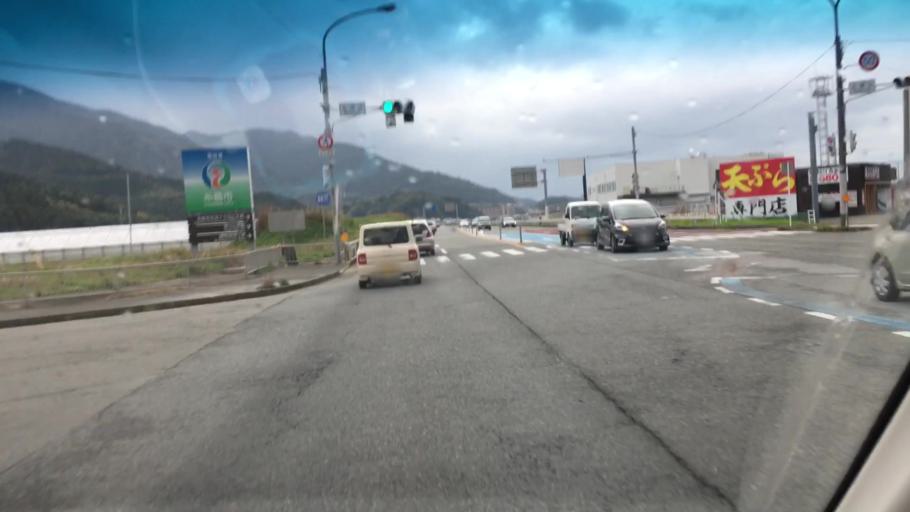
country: JP
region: Fukuoka
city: Maebaru-chuo
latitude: 33.5169
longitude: 130.1543
